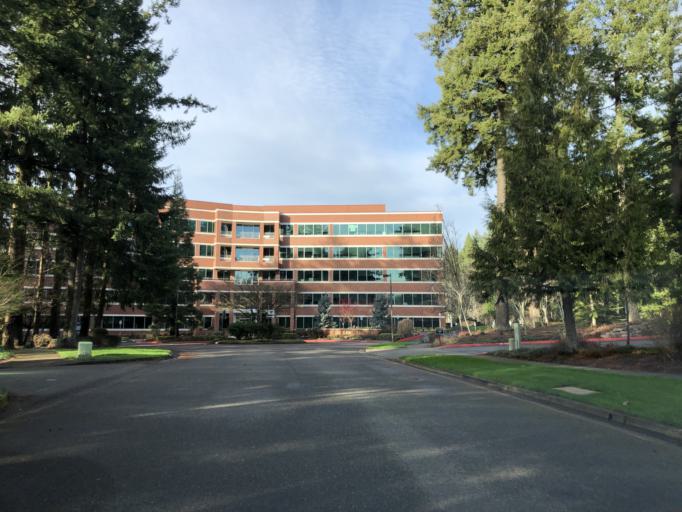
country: US
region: Oregon
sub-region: Washington County
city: Durham
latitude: 45.4228
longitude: -122.7399
